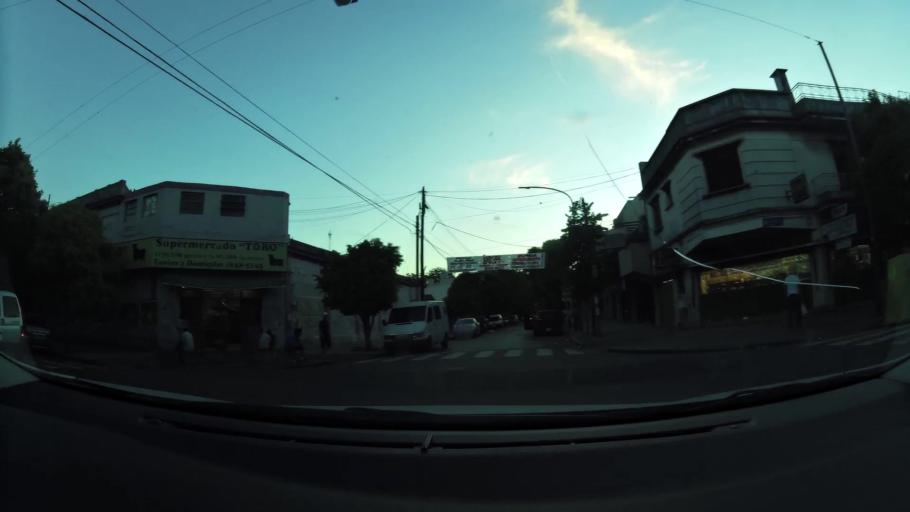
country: AR
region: Buenos Aires F.D.
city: Villa Lugano
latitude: -34.6778
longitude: -58.4746
